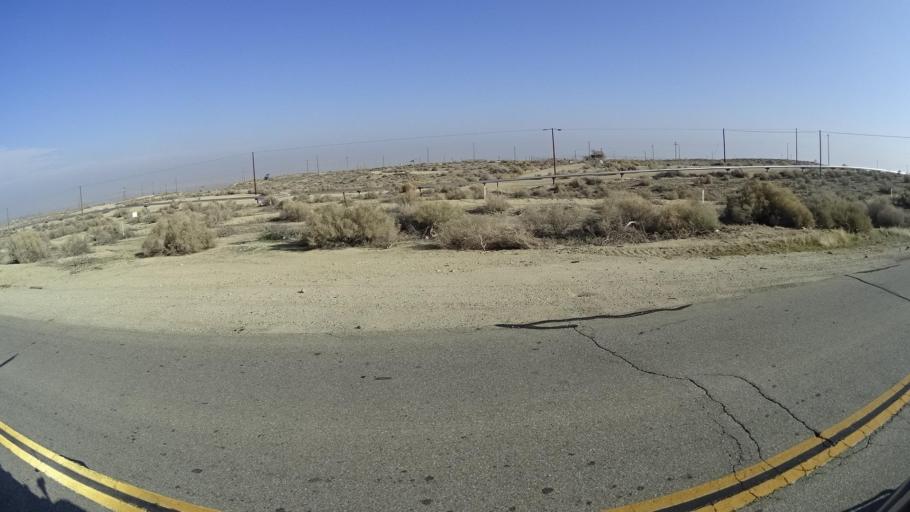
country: US
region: California
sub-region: Kern County
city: Taft Heights
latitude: 35.1660
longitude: -119.5316
